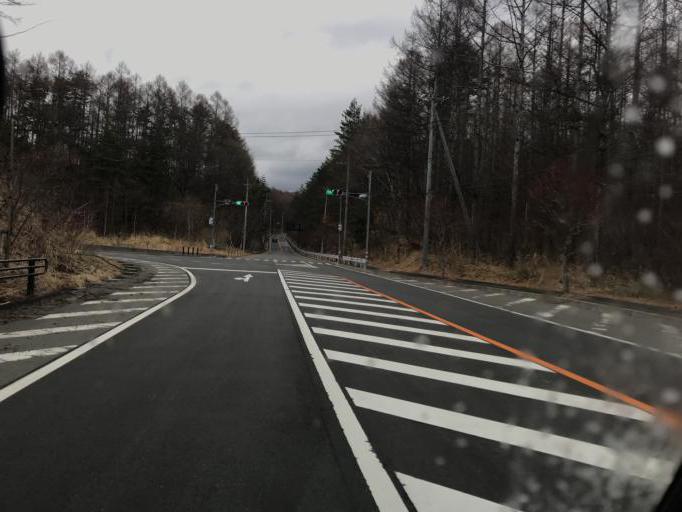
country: JP
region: Nagano
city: Chino
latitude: 35.8934
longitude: 138.3258
